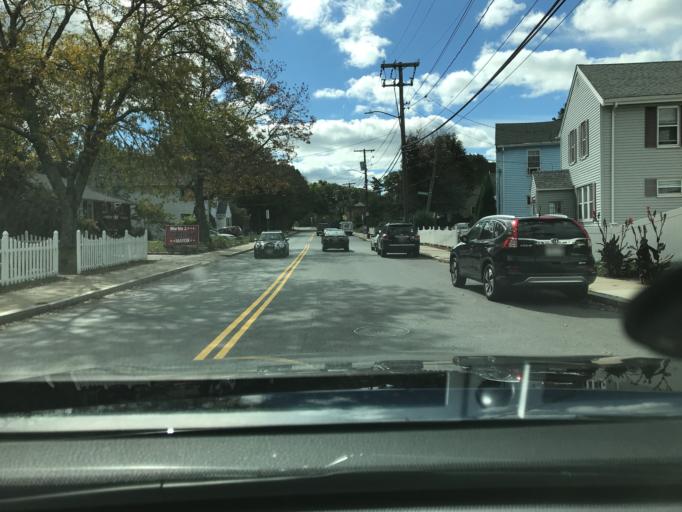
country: US
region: Massachusetts
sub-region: Norfolk County
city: Dedham
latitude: 42.2709
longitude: -71.1620
